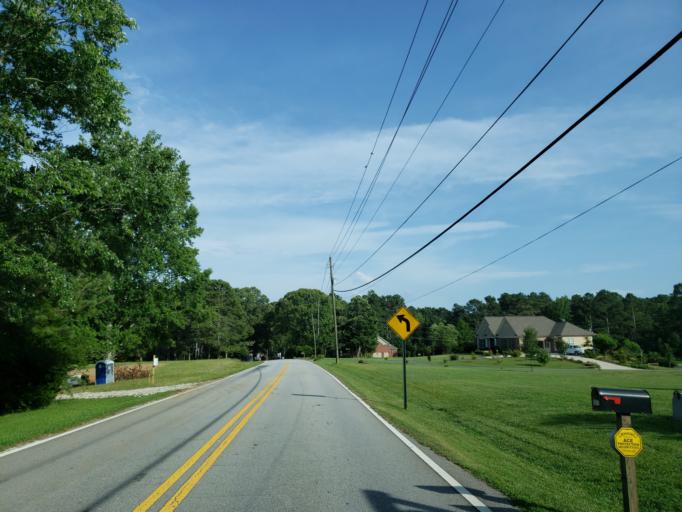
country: US
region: Georgia
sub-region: Paulding County
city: Hiram
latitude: 33.9136
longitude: -84.7168
